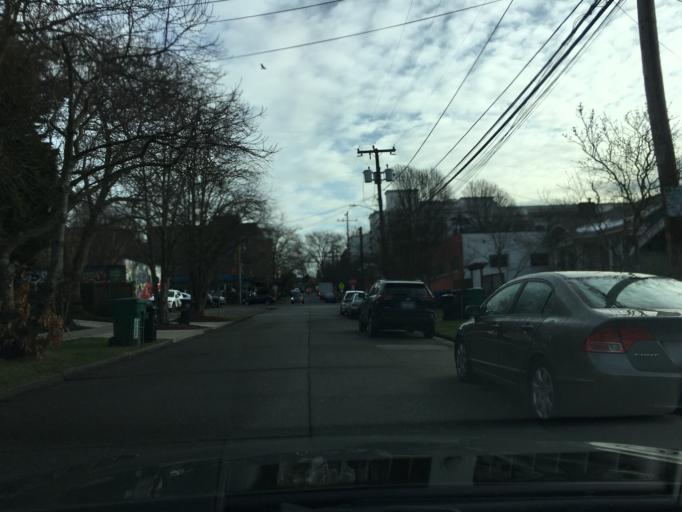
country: US
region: Washington
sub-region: King County
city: Seattle
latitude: 47.6607
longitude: -122.3433
